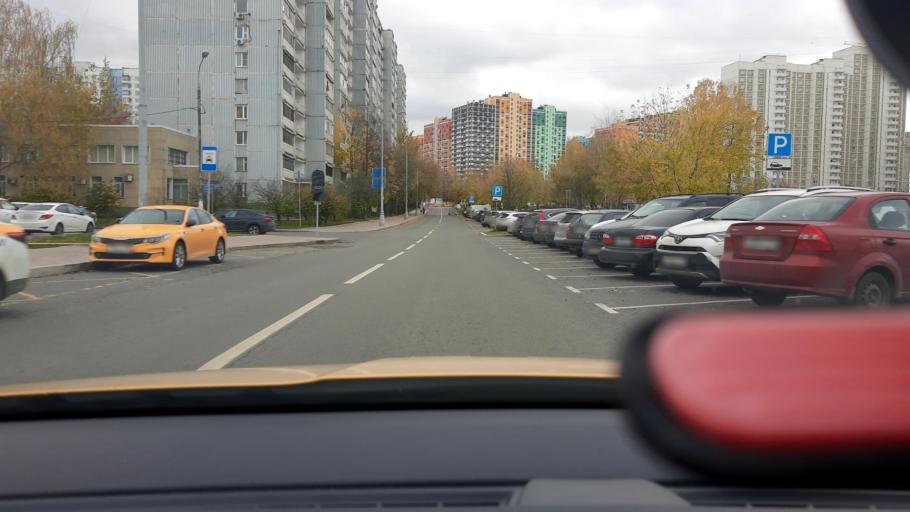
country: RU
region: Moscow
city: Solntsevo
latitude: 55.6498
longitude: 37.3928
